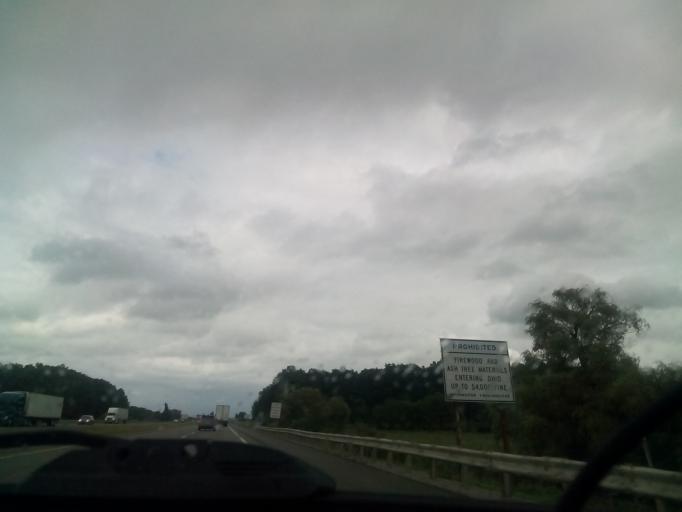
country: US
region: Indiana
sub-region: Steuben County
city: Hamilton
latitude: 41.6287
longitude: -84.8037
